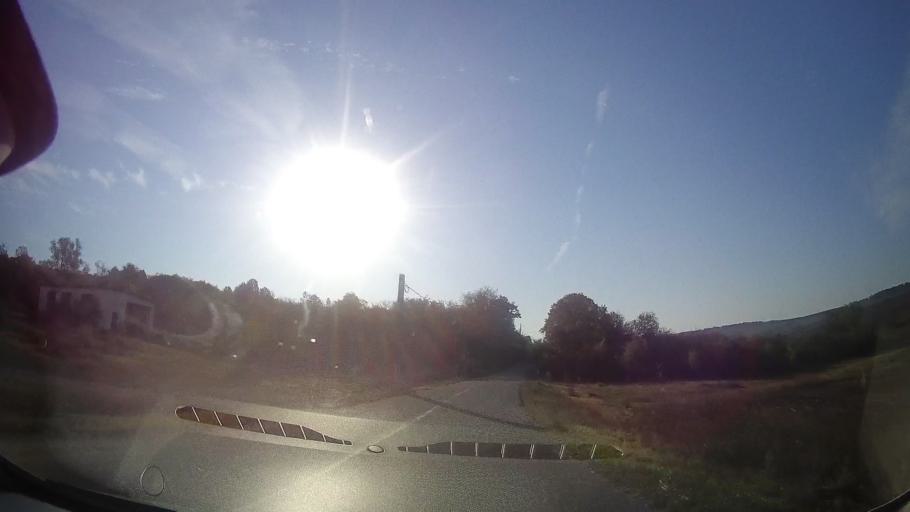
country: RO
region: Timis
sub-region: Comuna Bogda
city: Bogda
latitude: 45.9655
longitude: 21.6106
